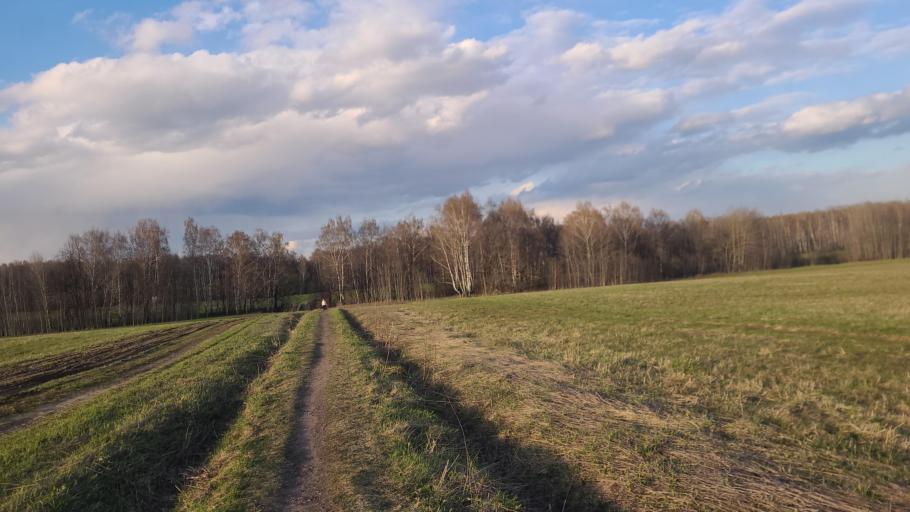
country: RU
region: Moskovskaya
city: Belyye Stolby
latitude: 55.3074
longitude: 37.8663
